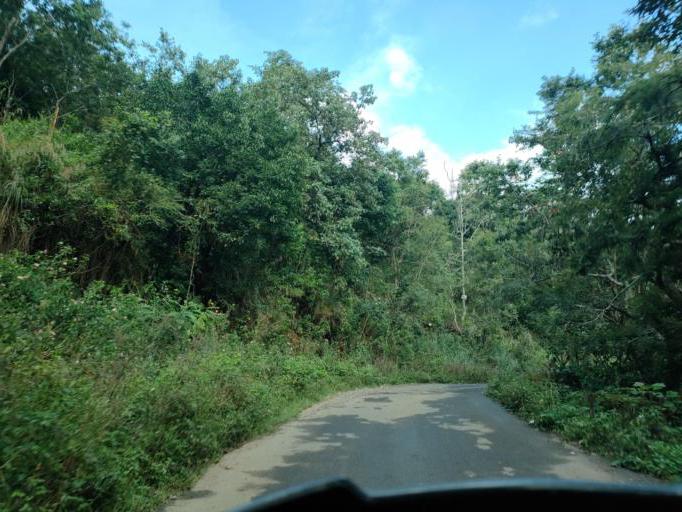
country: IN
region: Tamil Nadu
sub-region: Dindigul
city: Kodaikanal
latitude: 10.2872
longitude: 77.5297
